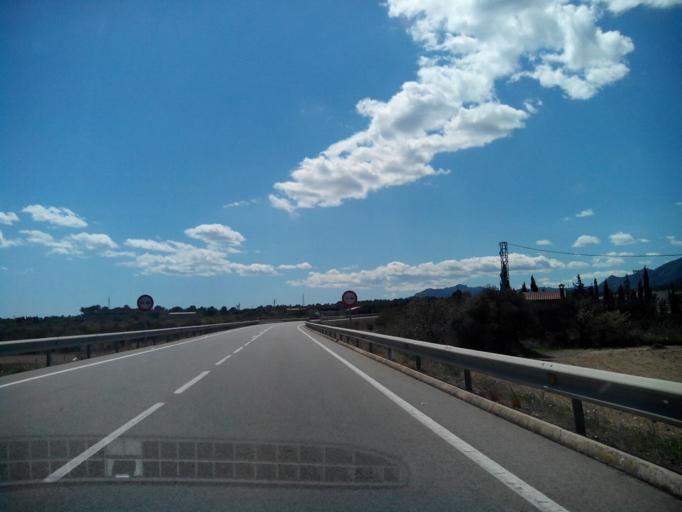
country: ES
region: Catalonia
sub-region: Provincia de Tarragona
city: Vilanova d'Escornalbou
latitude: 41.0856
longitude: 0.9691
